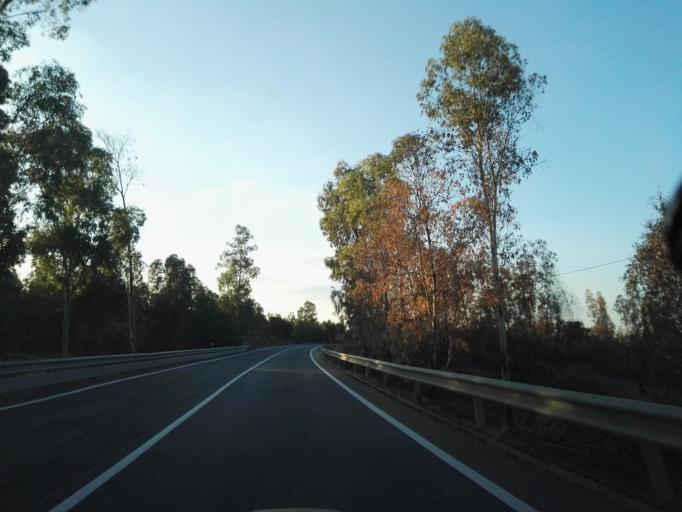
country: PT
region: Evora
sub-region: Arraiolos
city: Arraiolos
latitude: 38.8813
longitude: -7.9980
